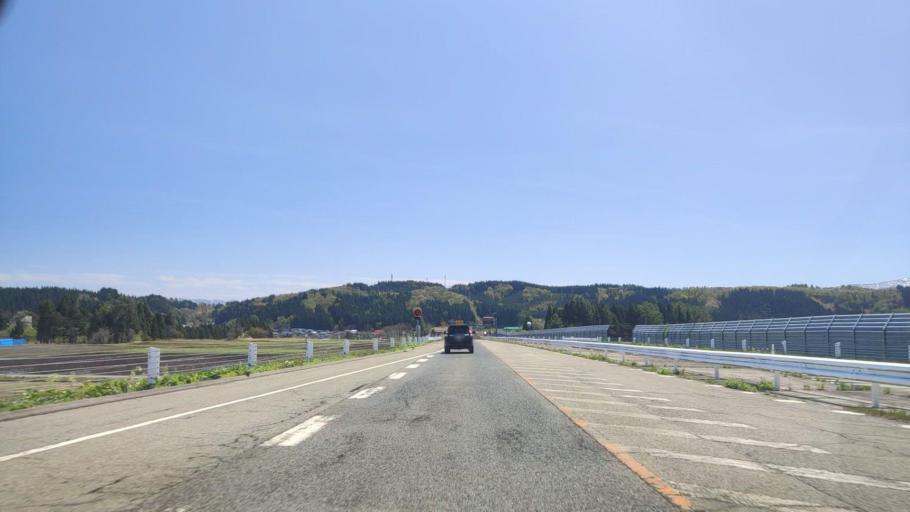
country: JP
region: Yamagata
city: Shinjo
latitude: 38.6998
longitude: 140.3103
